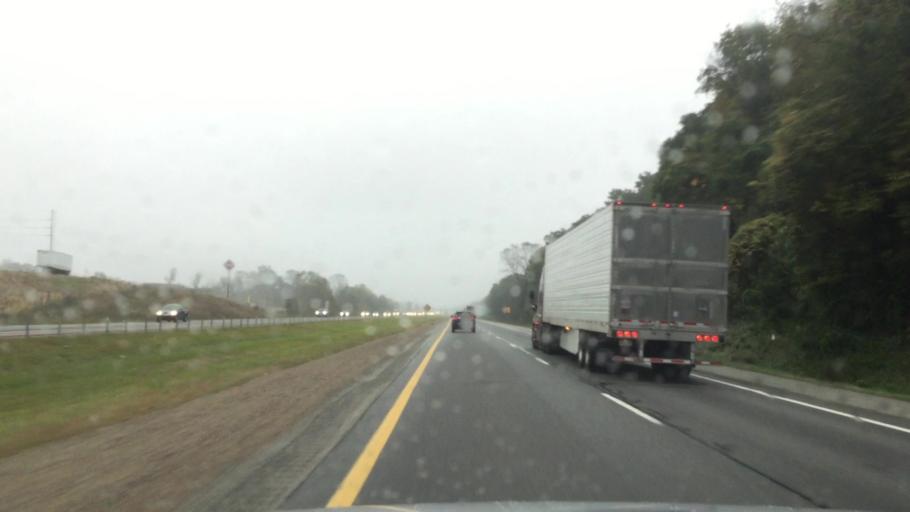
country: US
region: Michigan
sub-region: Kalamazoo County
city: Westwood
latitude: 42.2377
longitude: -85.6943
